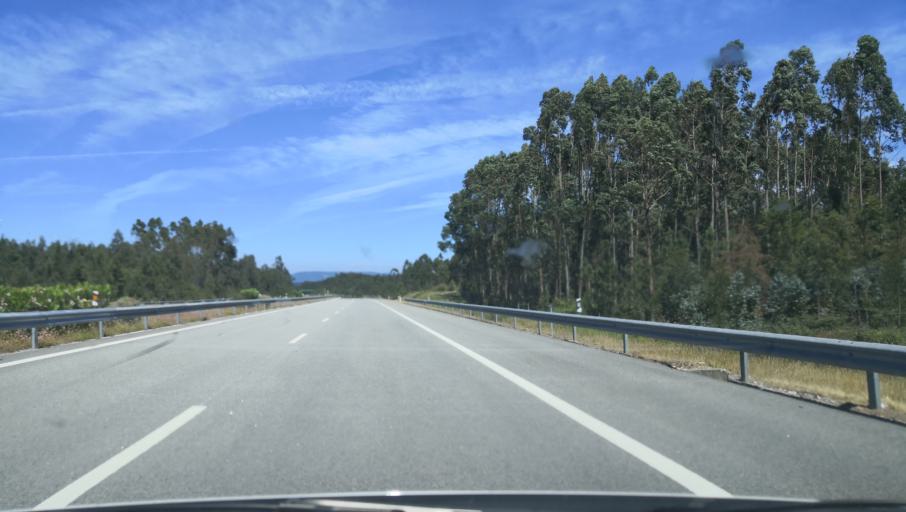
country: PT
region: Coimbra
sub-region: Montemor-O-Velho
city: Arazede
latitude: 40.2725
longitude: -8.6013
